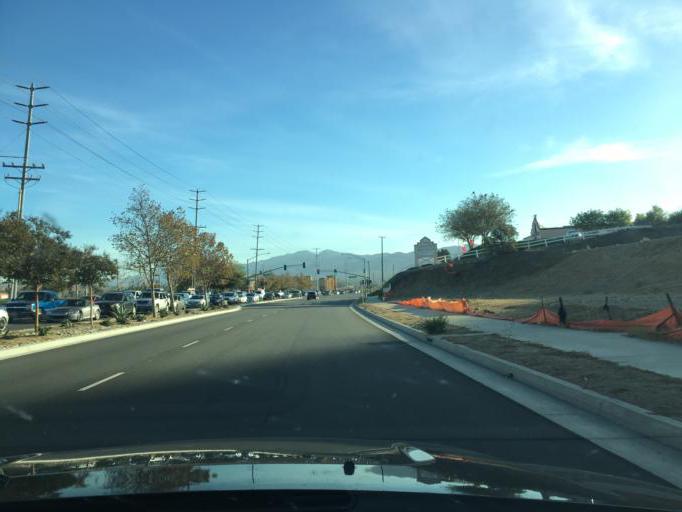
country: US
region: California
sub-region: Riverside County
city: Norco
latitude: 33.9359
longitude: -117.5574
